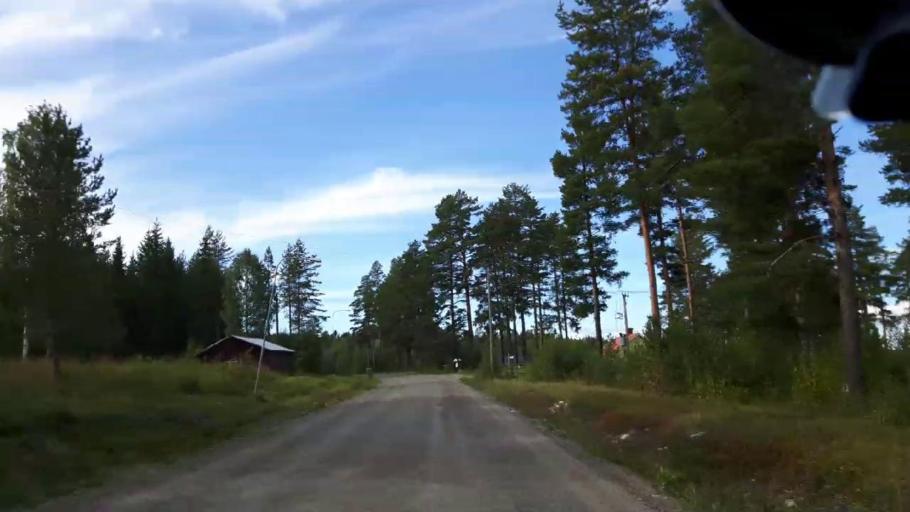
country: SE
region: Jaemtland
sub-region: Ragunda Kommun
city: Hammarstrand
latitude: 63.1369
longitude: 16.2521
